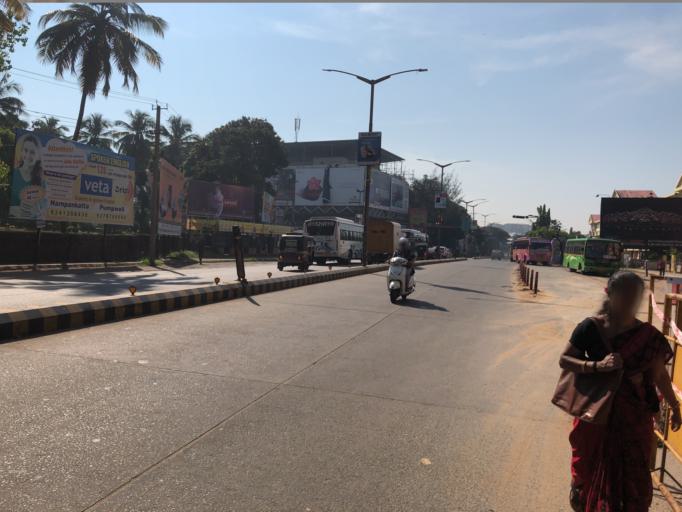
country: IN
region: Karnataka
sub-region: Dakshina Kannada
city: Mangalore
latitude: 12.8862
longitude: 74.8387
